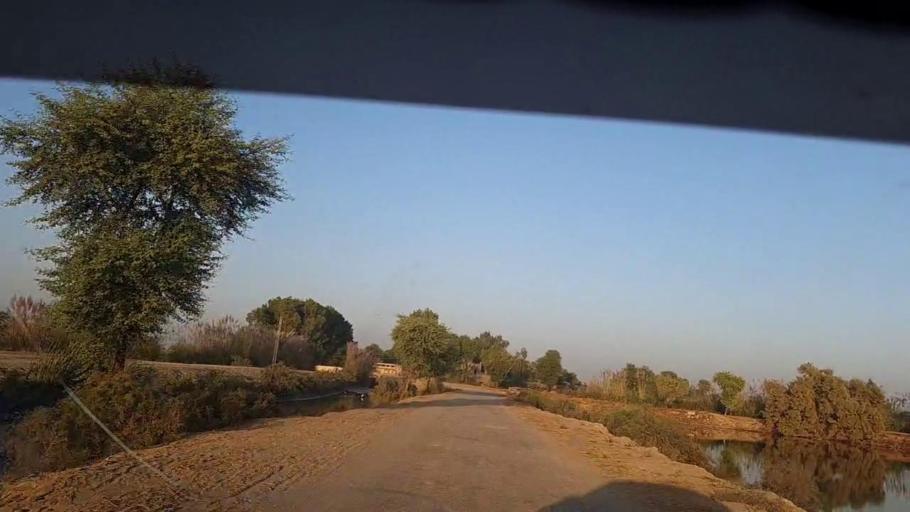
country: PK
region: Sindh
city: Ratodero
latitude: 27.9039
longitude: 68.2382
